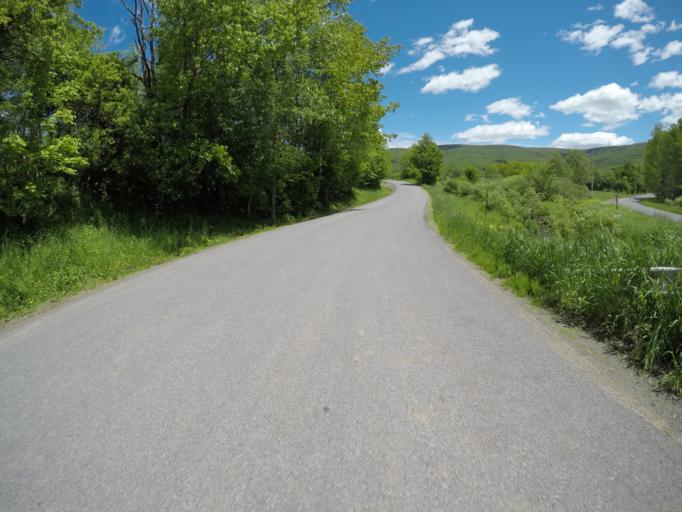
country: US
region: New York
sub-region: Delaware County
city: Stamford
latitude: 42.2590
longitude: -74.5228
